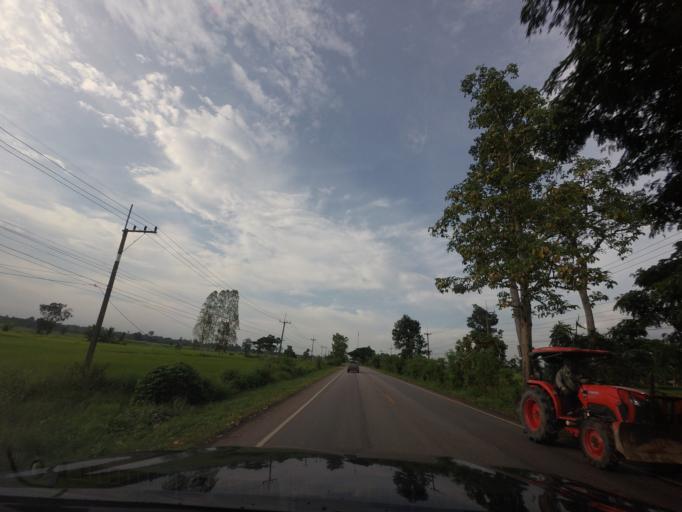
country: TH
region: Changwat Udon Thani
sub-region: Amphoe Ban Phue
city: Ban Phue
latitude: 17.7618
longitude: 102.3975
